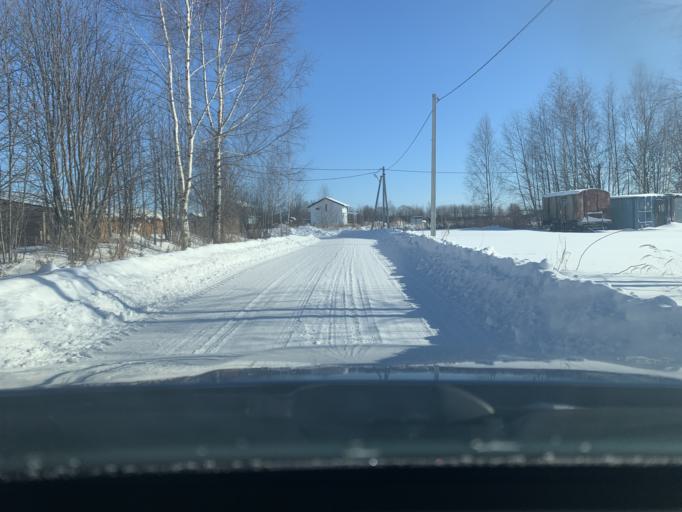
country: RU
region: Jaroslavl
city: Tunoshna
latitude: 57.6510
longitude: 40.0668
